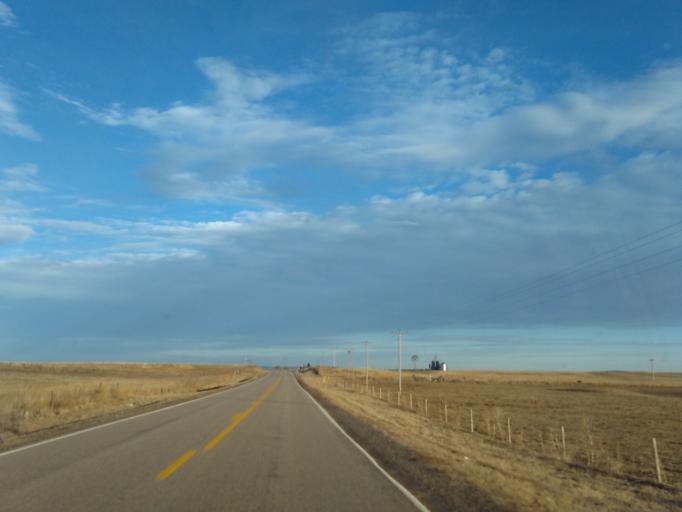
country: US
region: Nebraska
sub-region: Morrill County
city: Bridgeport
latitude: 41.5982
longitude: -102.9667
